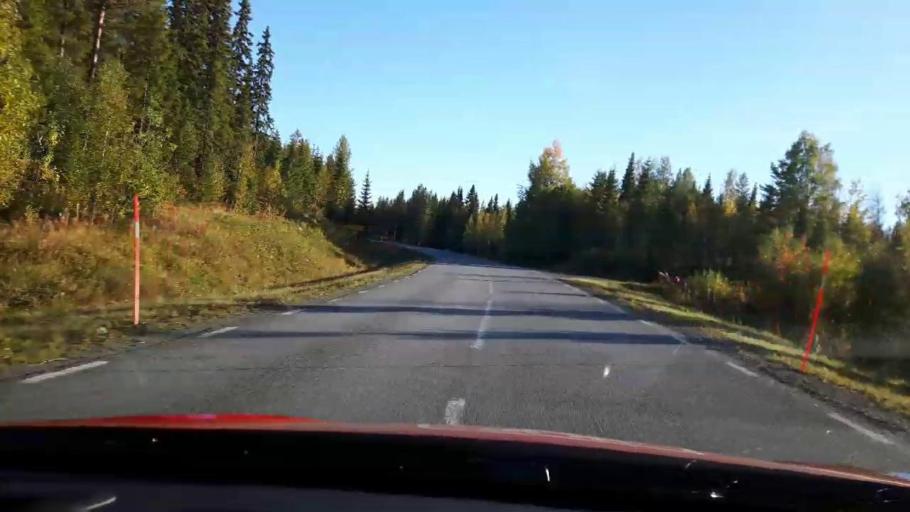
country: SE
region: Jaemtland
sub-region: OEstersunds Kommun
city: Lit
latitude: 63.7935
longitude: 14.7031
